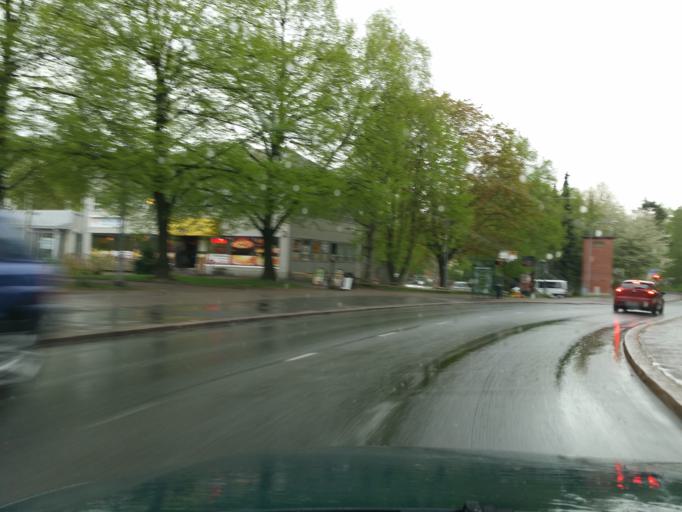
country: FI
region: Uusimaa
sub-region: Helsinki
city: Teekkarikylae
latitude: 60.2301
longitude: 24.8951
